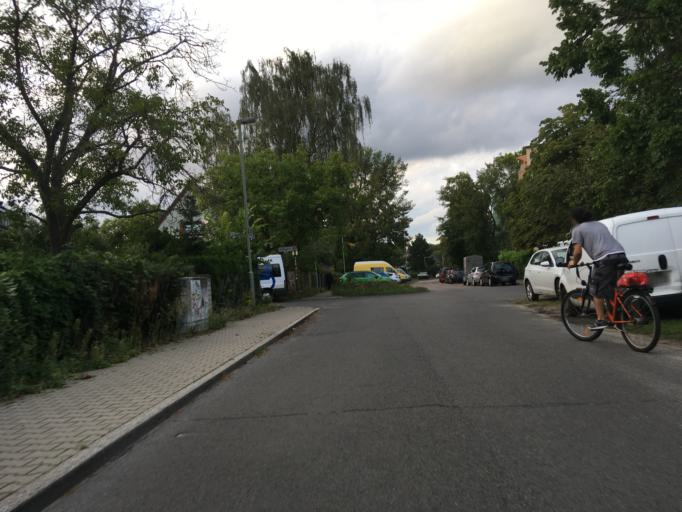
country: DE
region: Berlin
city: Johannisthal
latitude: 52.4455
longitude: 13.5008
